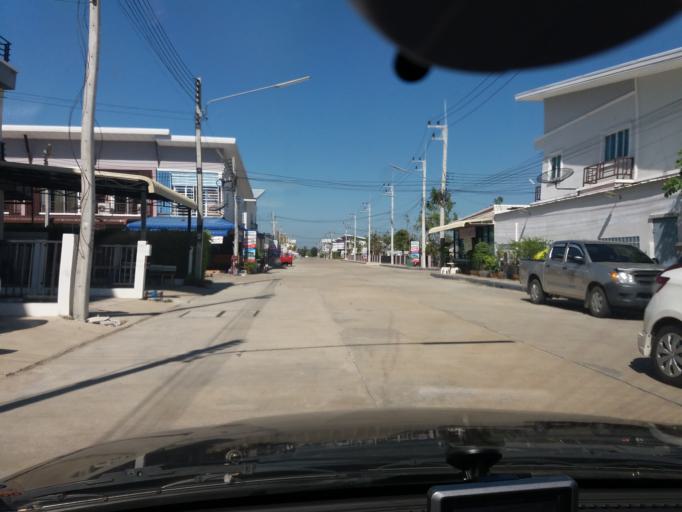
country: TH
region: Suphan Buri
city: Suphan Buri
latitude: 14.4586
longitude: 100.1457
